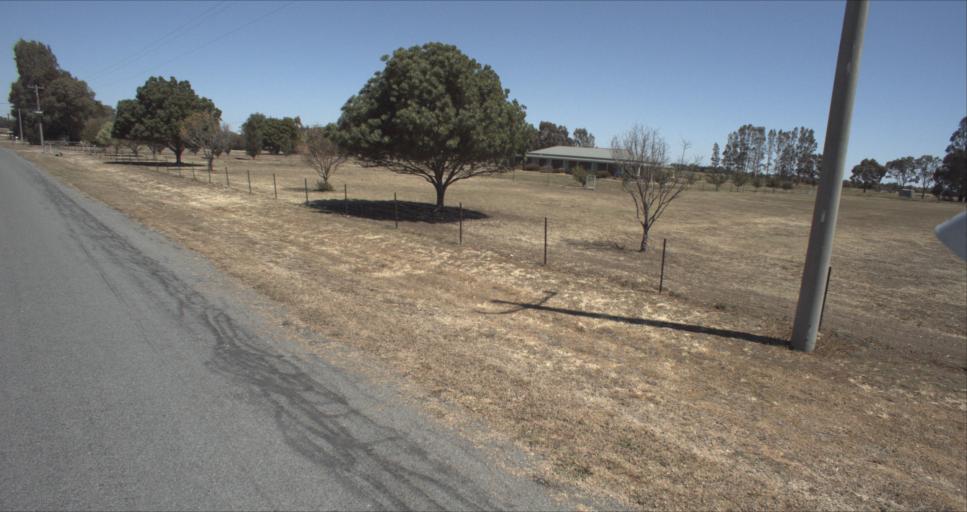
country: AU
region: New South Wales
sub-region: Leeton
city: Leeton
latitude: -34.5195
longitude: 146.4040
